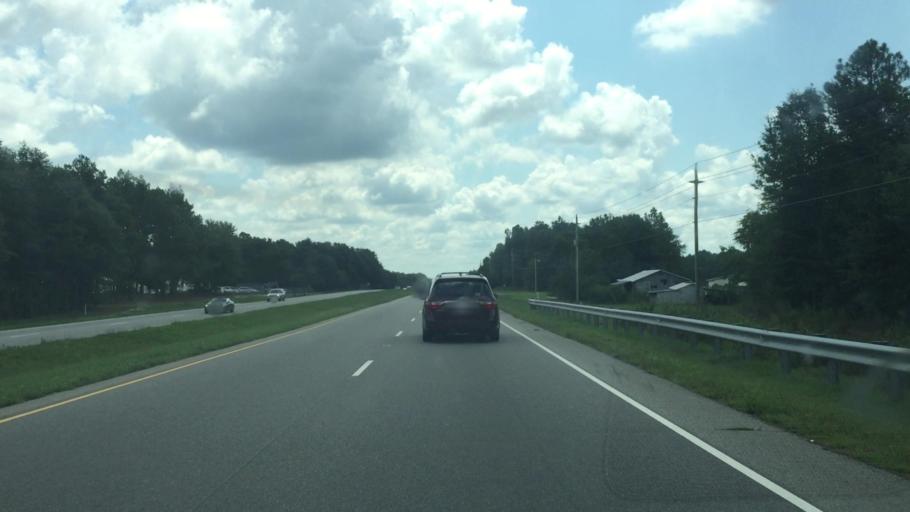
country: US
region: North Carolina
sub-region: Scotland County
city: Laurel Hill
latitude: 34.8264
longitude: -79.5895
